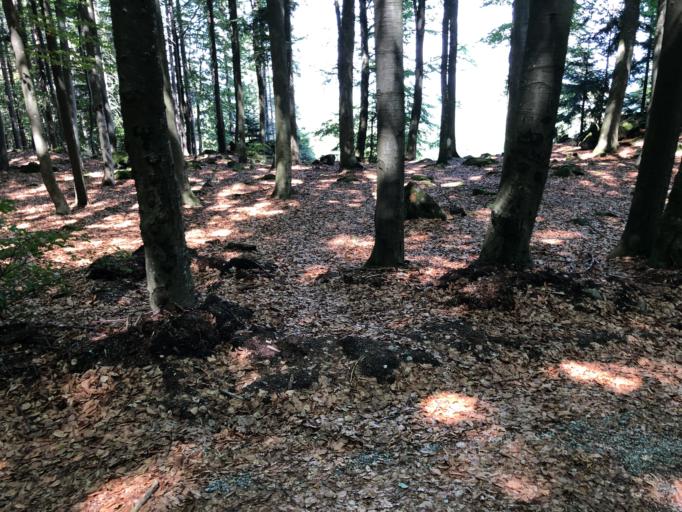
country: DE
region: Bavaria
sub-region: Upper Palatinate
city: Neukirchen
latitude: 49.2434
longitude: 12.9451
